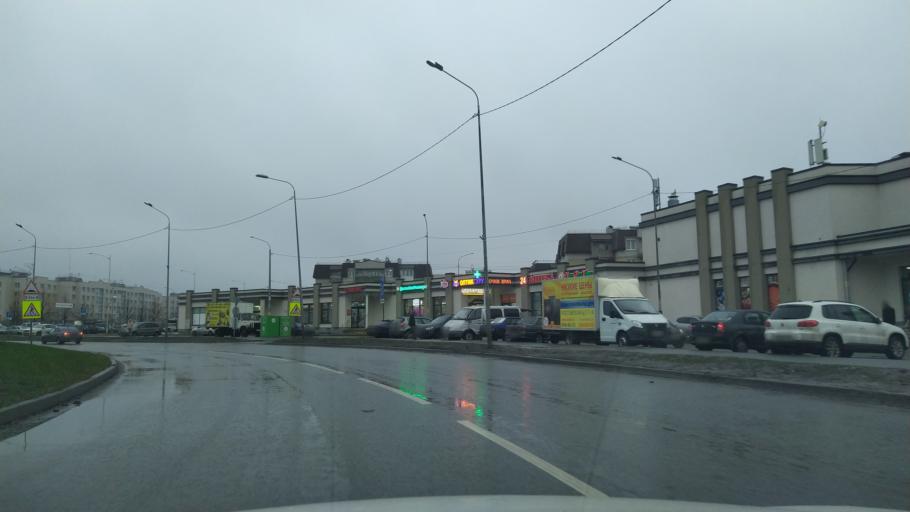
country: RU
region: St.-Petersburg
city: Tyarlevo
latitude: 59.7380
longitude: 30.4643
